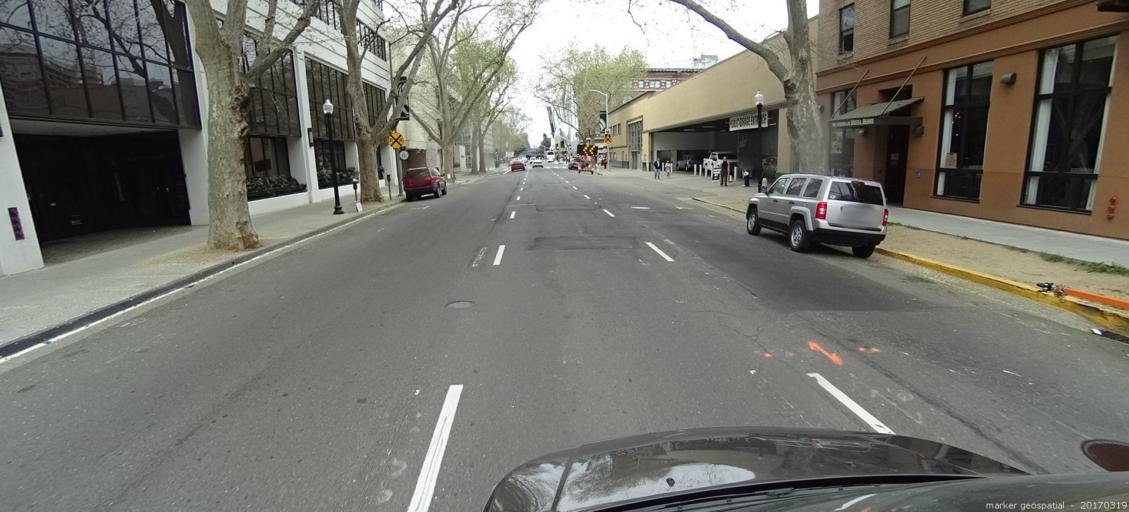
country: US
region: California
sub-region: Sacramento County
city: Sacramento
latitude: 38.5788
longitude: -121.4971
